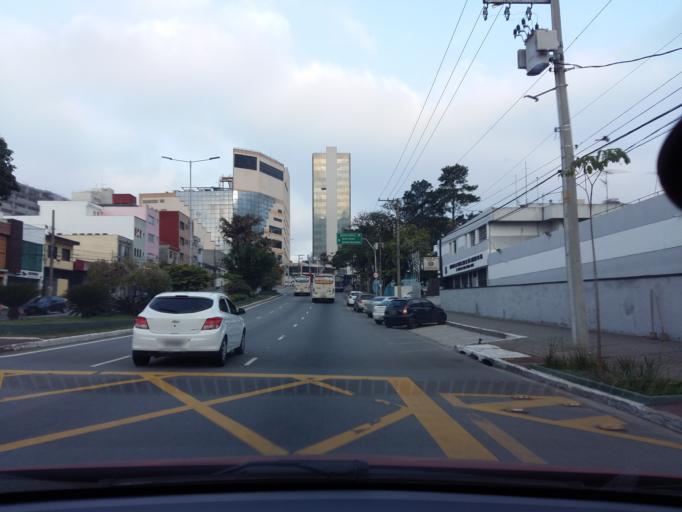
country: BR
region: Sao Paulo
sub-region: Sao Caetano Do Sul
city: Sao Caetano do Sul
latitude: -23.6154
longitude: -46.5754
